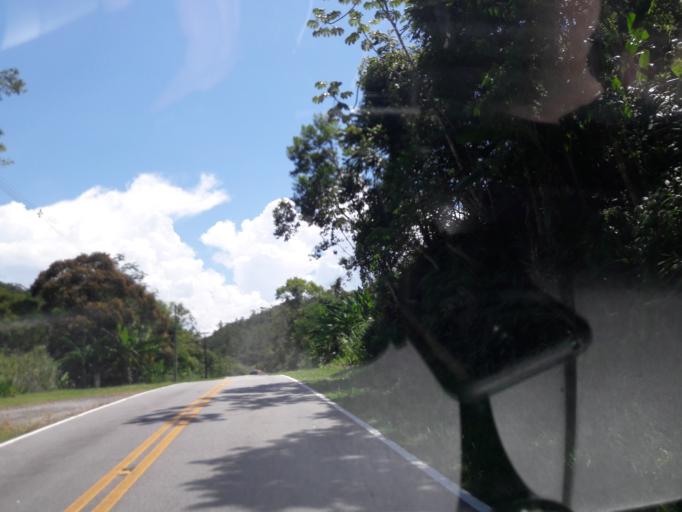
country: BR
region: Parana
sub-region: Antonina
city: Antonina
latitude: -25.5241
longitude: -48.7656
